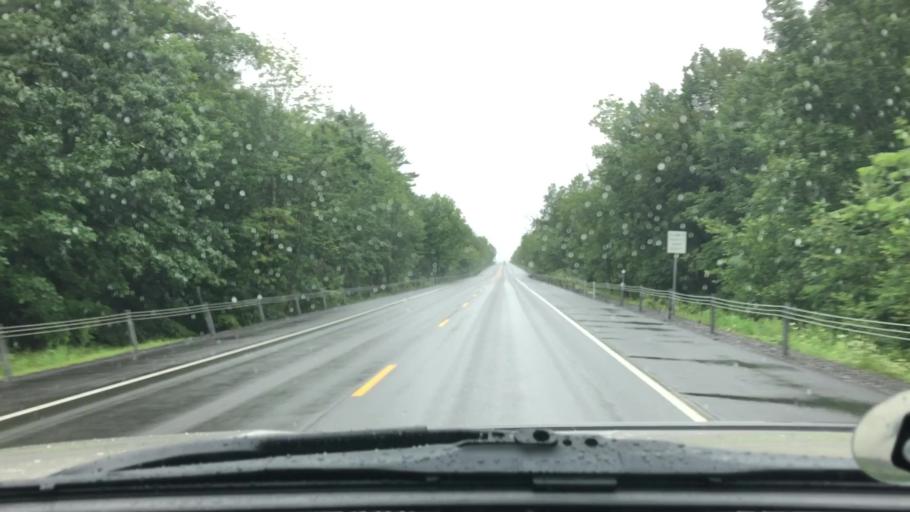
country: US
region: New York
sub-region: Greene County
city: Cairo
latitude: 42.3048
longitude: -74.0425
